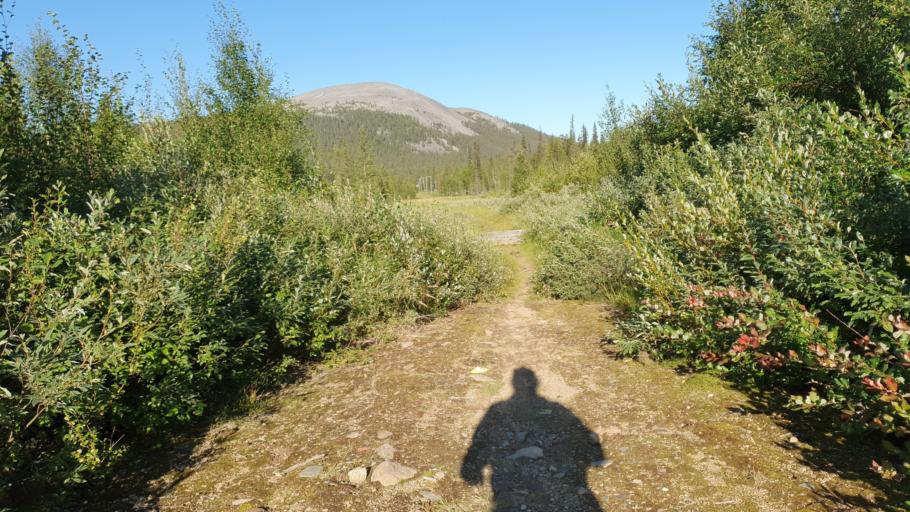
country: FI
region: Lapland
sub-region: Tunturi-Lappi
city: Kolari
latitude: 67.5991
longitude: 24.2066
